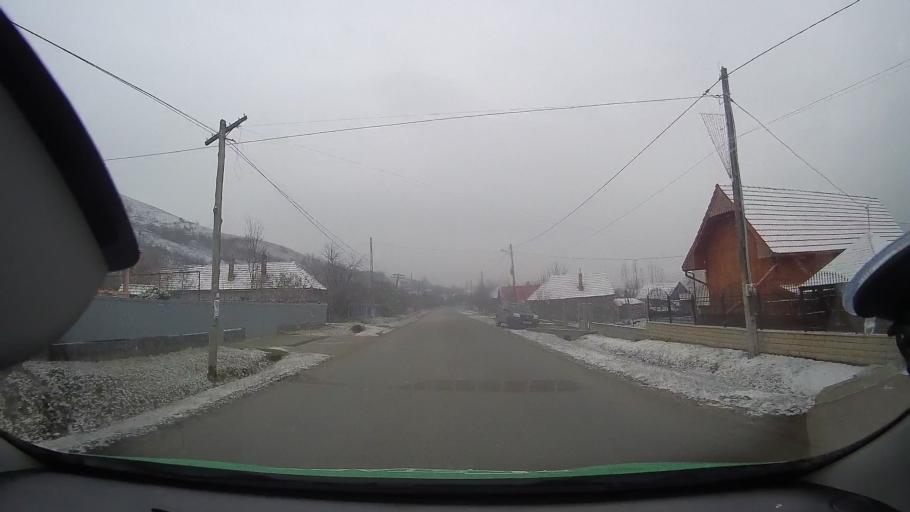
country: RO
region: Alba
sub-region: Comuna Noslac
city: Noslac
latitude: 46.3492
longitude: 23.9375
